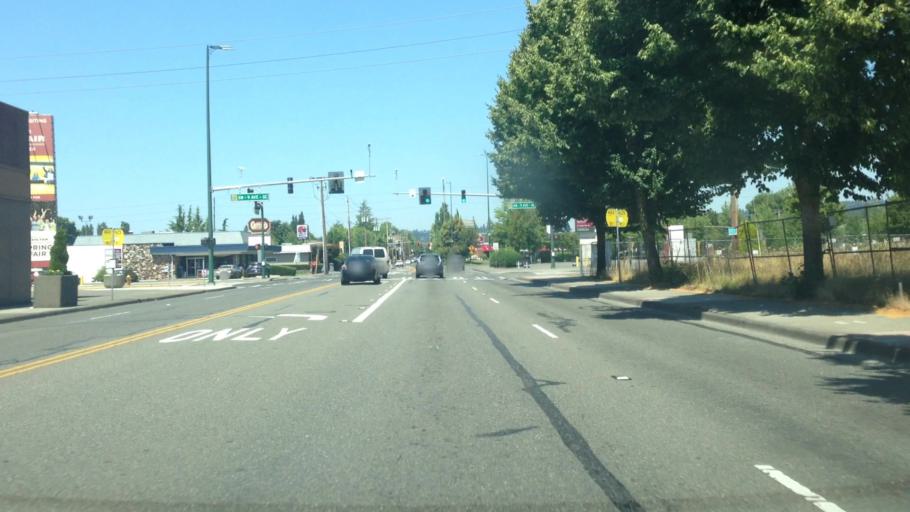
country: US
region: Washington
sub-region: Pierce County
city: Puyallup
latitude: 47.1838
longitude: -122.2936
